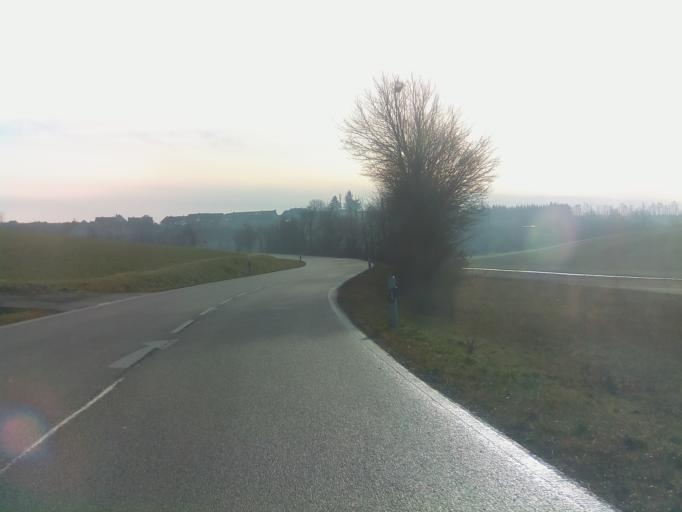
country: DE
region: Bavaria
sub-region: Regierungsbezirk Unterfranken
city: Waldbrunn
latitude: 49.7649
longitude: 9.7919
